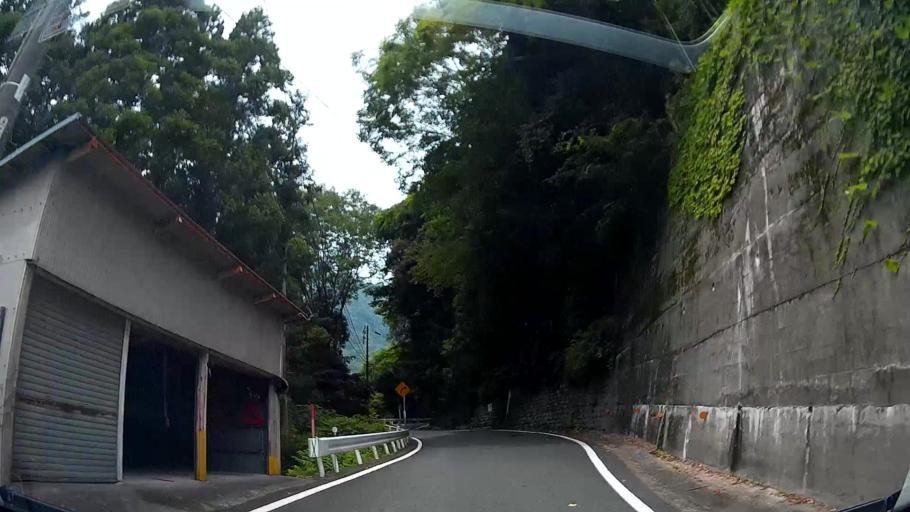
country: JP
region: Shizuoka
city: Hamakita
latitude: 35.0794
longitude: 137.7975
